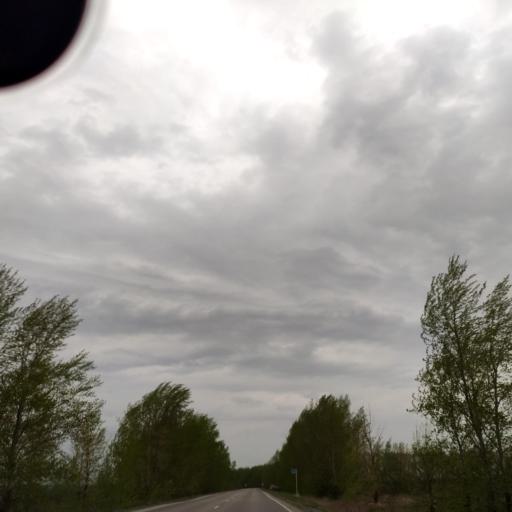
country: RU
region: Voronezj
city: Latnaya
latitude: 51.6971
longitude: 38.8234
